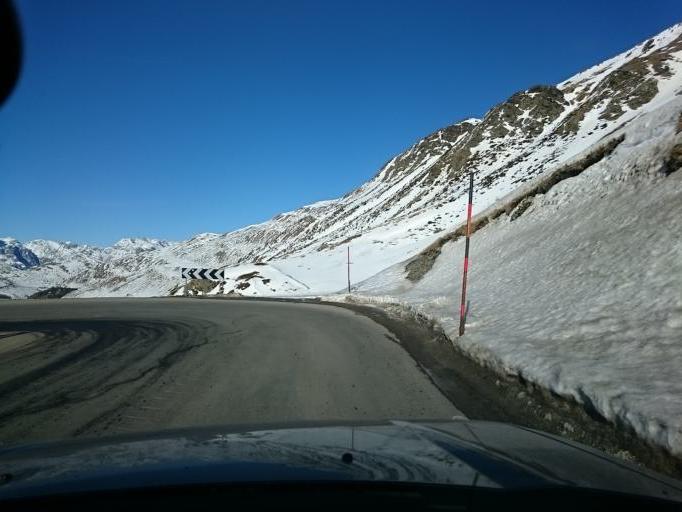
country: IT
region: Lombardy
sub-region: Provincia di Sondrio
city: Livigno
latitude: 46.4995
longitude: 10.2064
